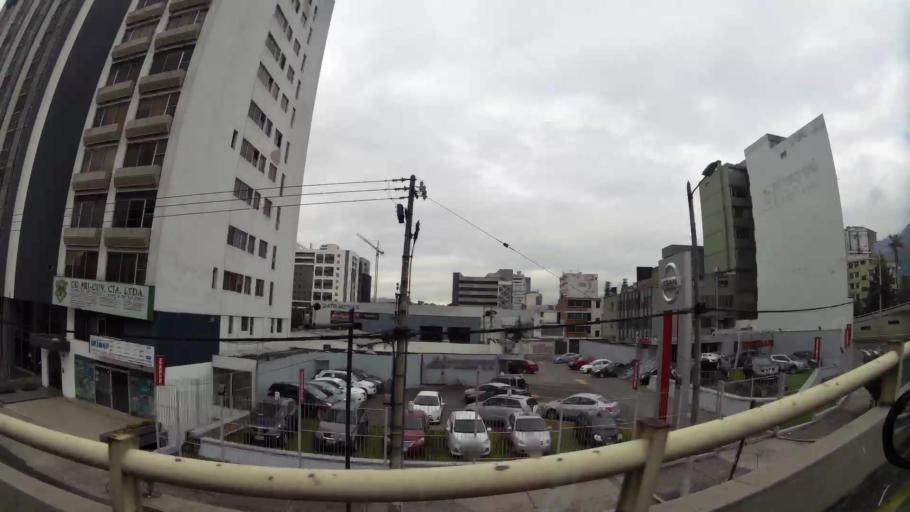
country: EC
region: Pichincha
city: Quito
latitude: -0.1960
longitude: -78.4945
